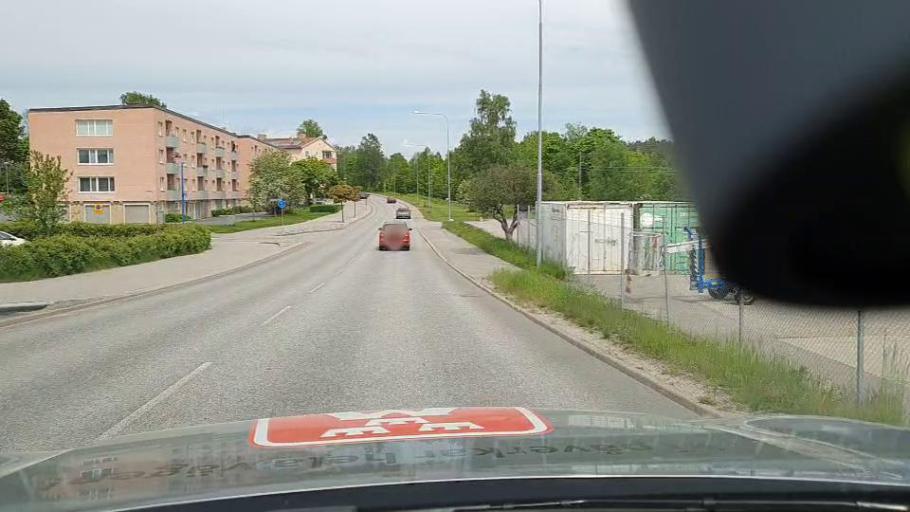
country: SE
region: Soedermanland
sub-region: Flens Kommun
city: Flen
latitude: 59.0535
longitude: 16.5952
